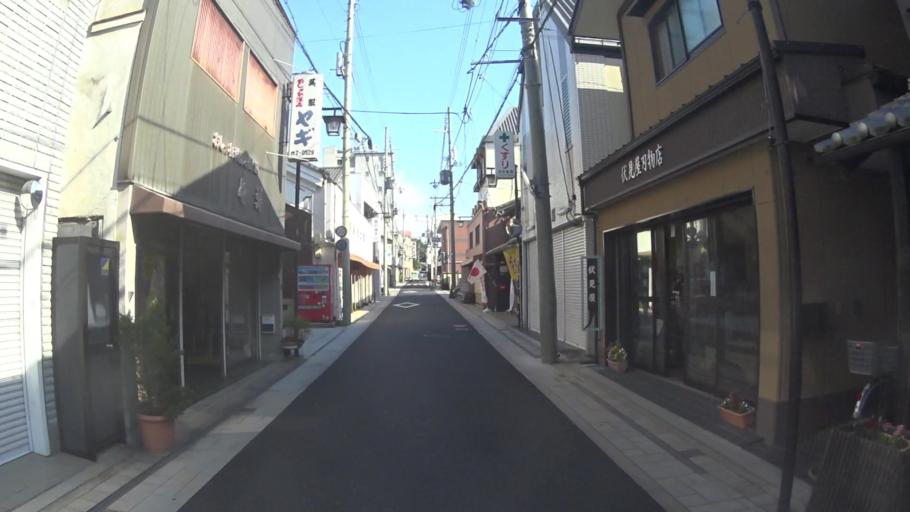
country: JP
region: Kyoto
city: Kameoka
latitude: 35.0153
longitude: 135.5768
